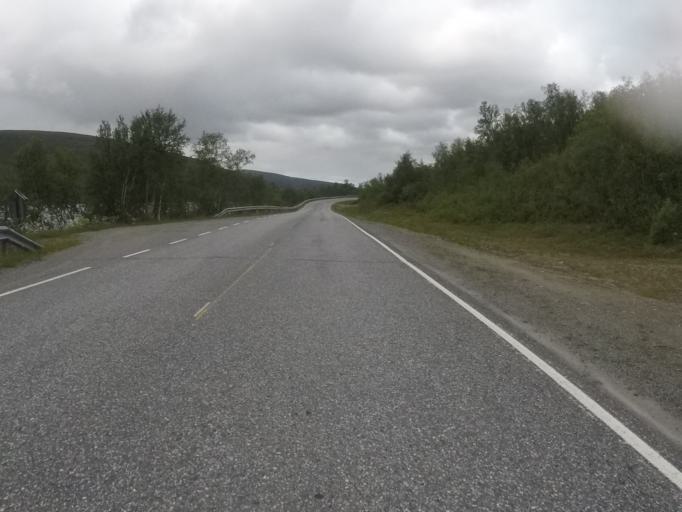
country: NO
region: Finnmark Fylke
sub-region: Alta
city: Alta
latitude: 69.6749
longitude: 23.4316
